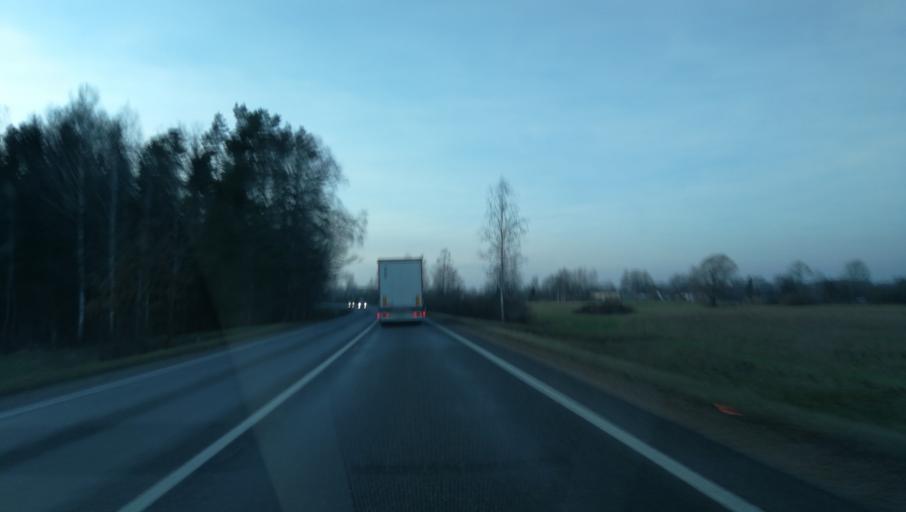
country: LV
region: Jaunpils
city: Jaunpils
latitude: 56.6640
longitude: 22.9850
